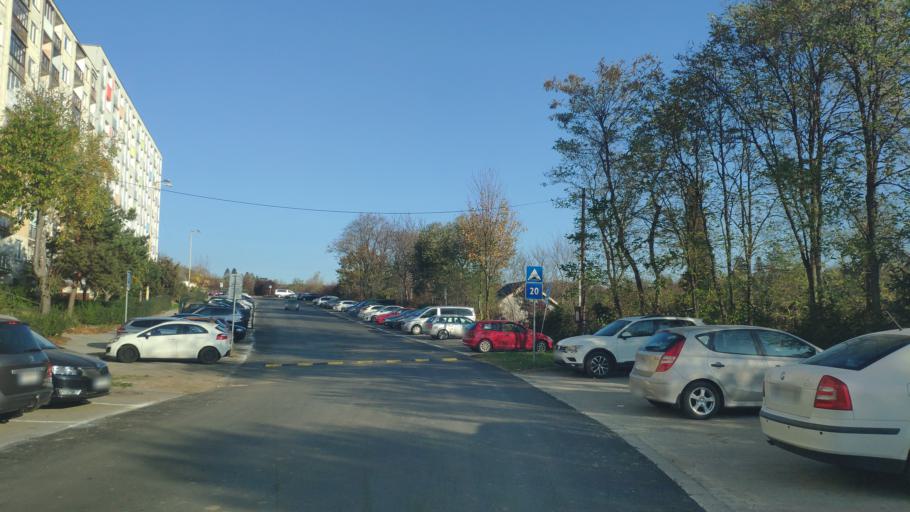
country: SK
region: Kosicky
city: Kosice
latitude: 48.7179
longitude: 21.2189
